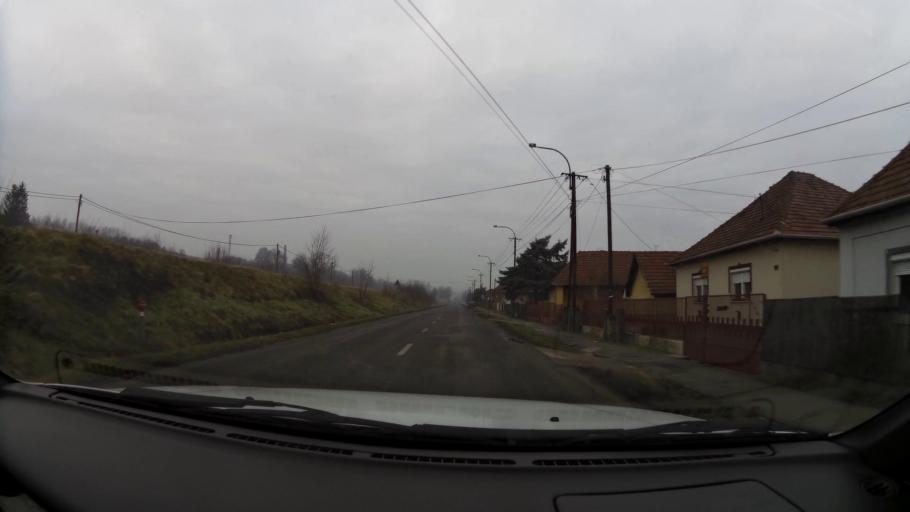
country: HU
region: Borsod-Abauj-Zemplen
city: Izsofalva
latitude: 48.3102
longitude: 20.6528
